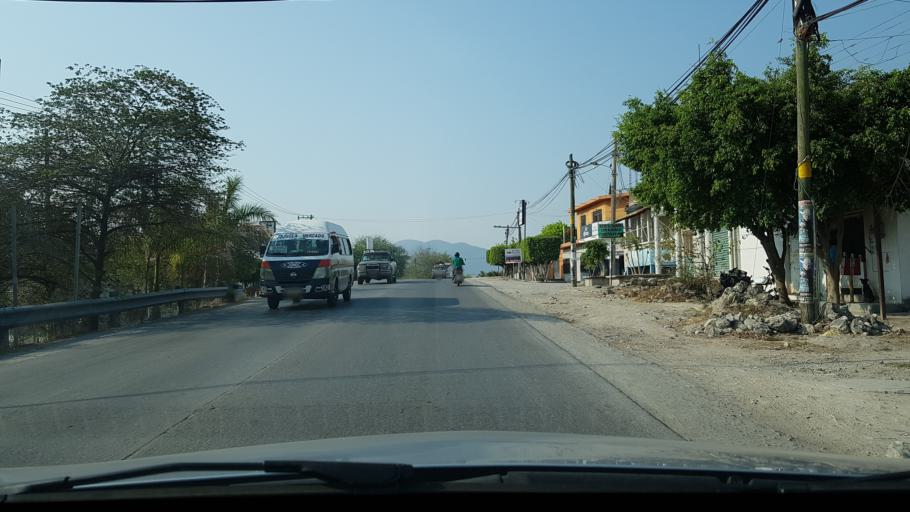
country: MX
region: Morelos
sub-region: Tlaquiltenango
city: Alfredo V. Bonfil (Chacampalco)
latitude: 18.6559
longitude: -99.1546
